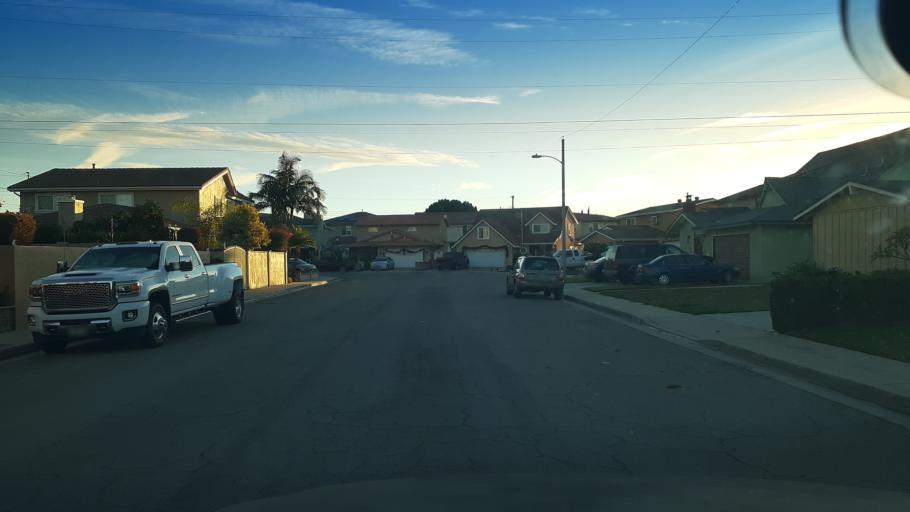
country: US
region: California
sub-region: Los Angeles County
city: Cerritos
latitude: 33.8573
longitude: -118.0746
